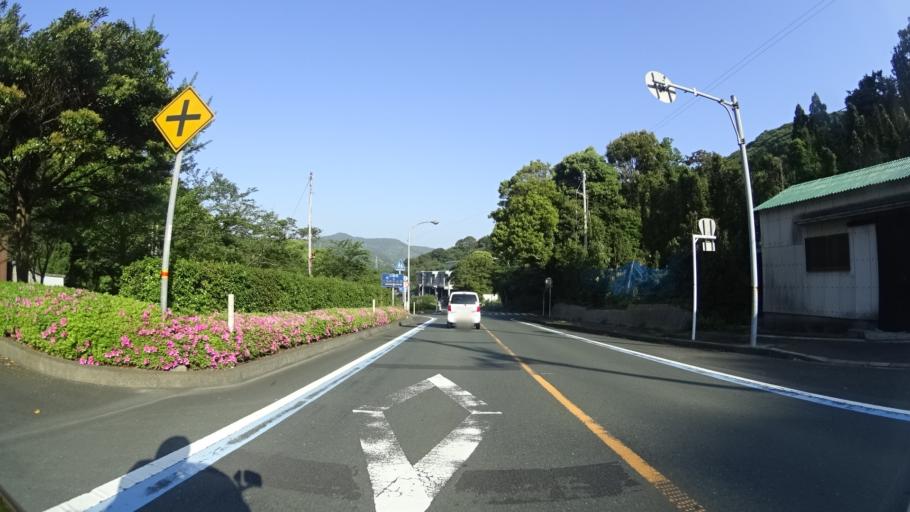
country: JP
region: Ehime
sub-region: Nishiuwa-gun
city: Ikata-cho
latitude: 33.3955
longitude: 132.1505
